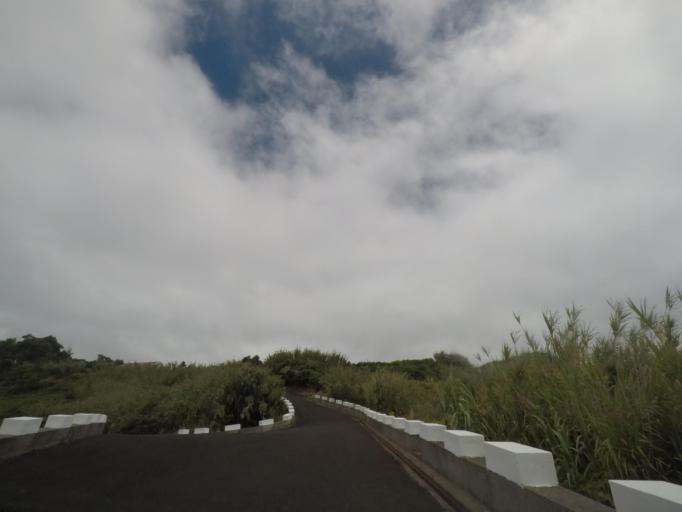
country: PT
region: Madeira
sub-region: Porto Moniz
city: Porto Moniz
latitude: 32.8593
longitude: -17.2029
